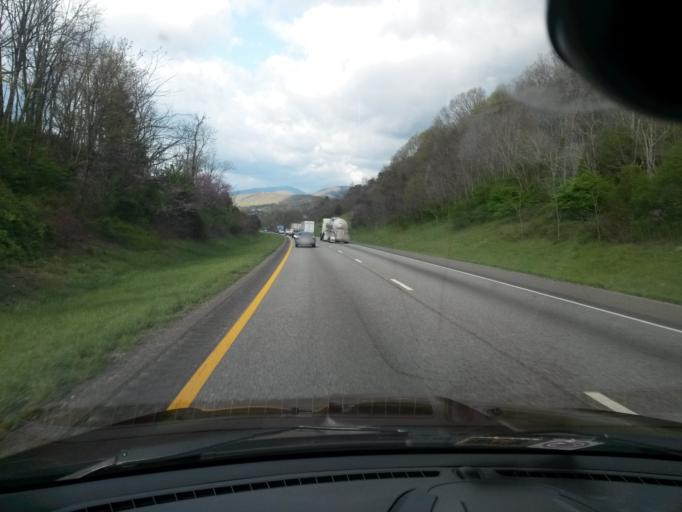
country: US
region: Virginia
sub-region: Roanoke County
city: Hollins
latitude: 37.3663
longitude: -79.9332
